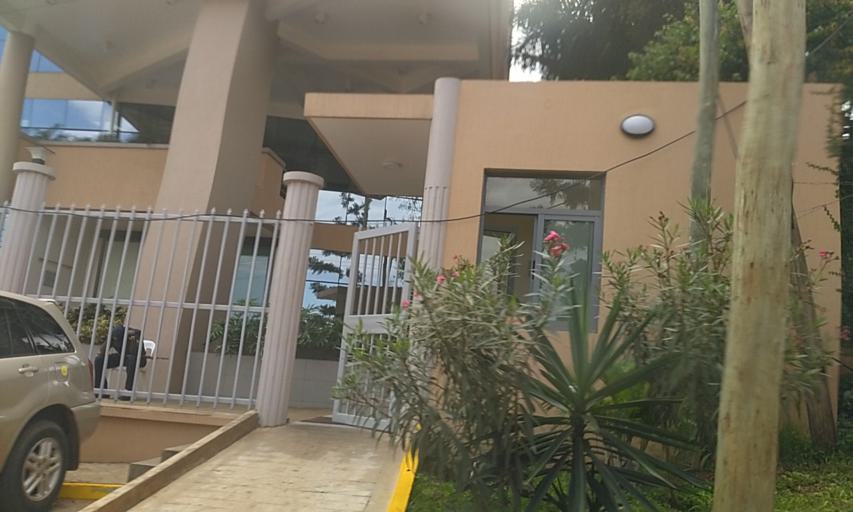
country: UG
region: Central Region
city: Kampala Central Division
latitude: 0.3419
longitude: 32.5913
